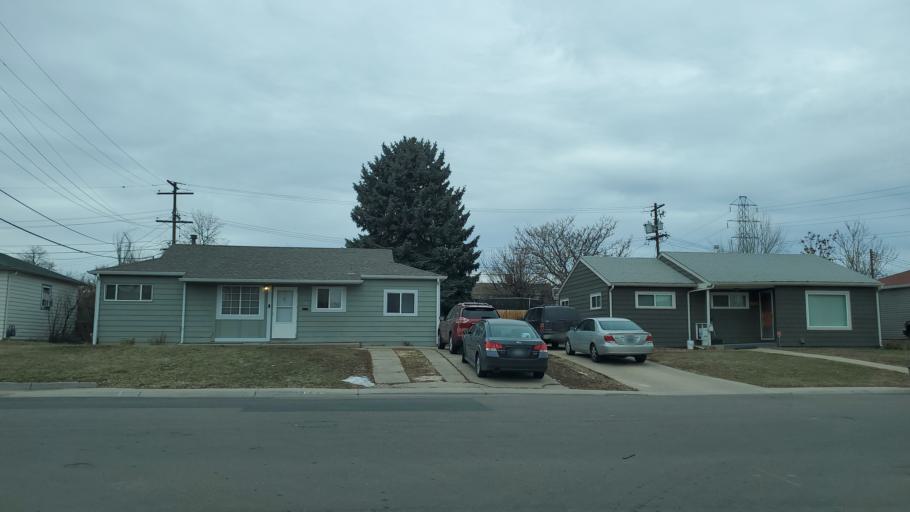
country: US
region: Colorado
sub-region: Denver County
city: Denver
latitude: 39.6958
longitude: -105.0106
